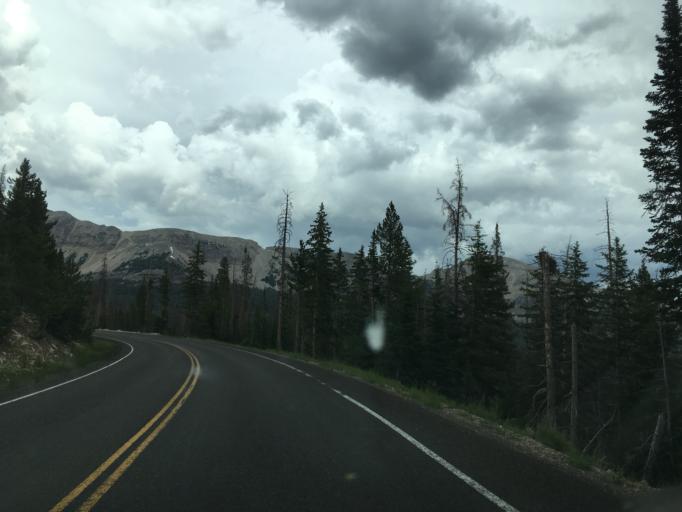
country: US
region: Utah
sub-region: Summit County
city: Kamas
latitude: 40.7123
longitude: -110.8779
